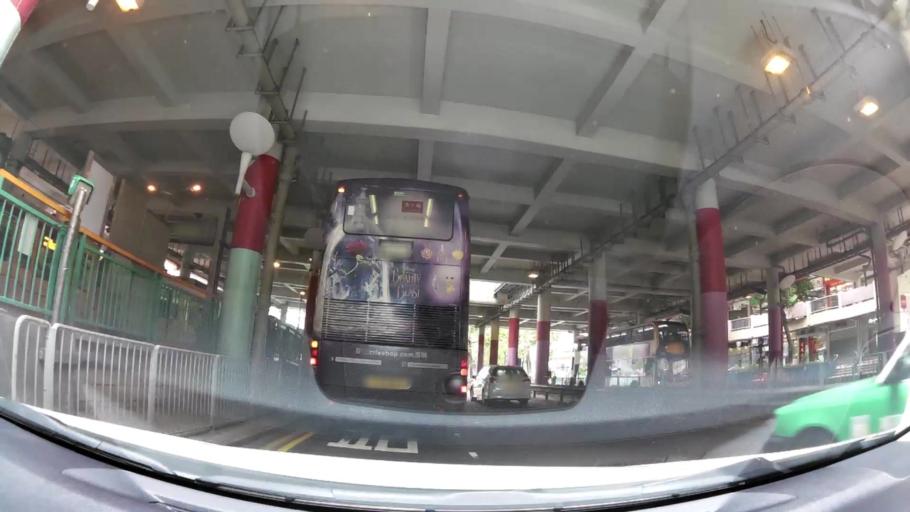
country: HK
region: Tuen Mun
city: Tuen Mun
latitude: 22.3875
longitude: 113.9752
